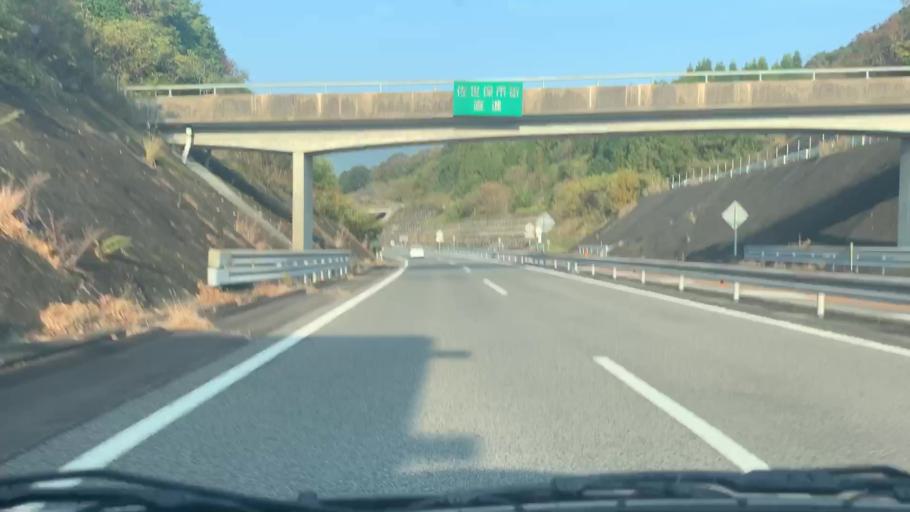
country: JP
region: Saga Prefecture
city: Imaricho-ko
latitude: 33.1677
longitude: 129.8557
